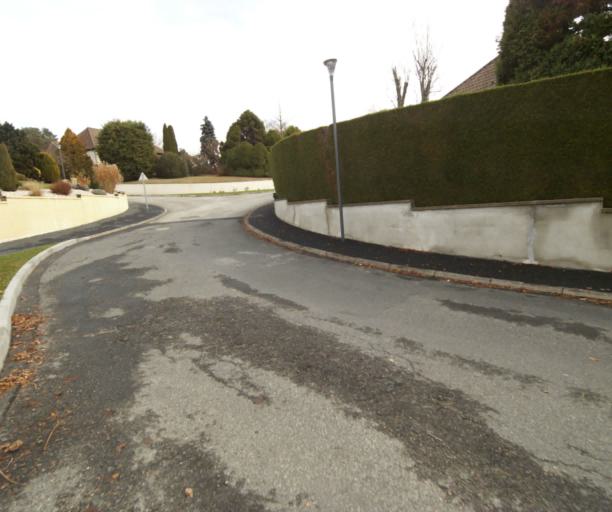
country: FR
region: Limousin
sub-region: Departement de la Correze
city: Chameyrat
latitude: 45.2594
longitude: 1.7002
